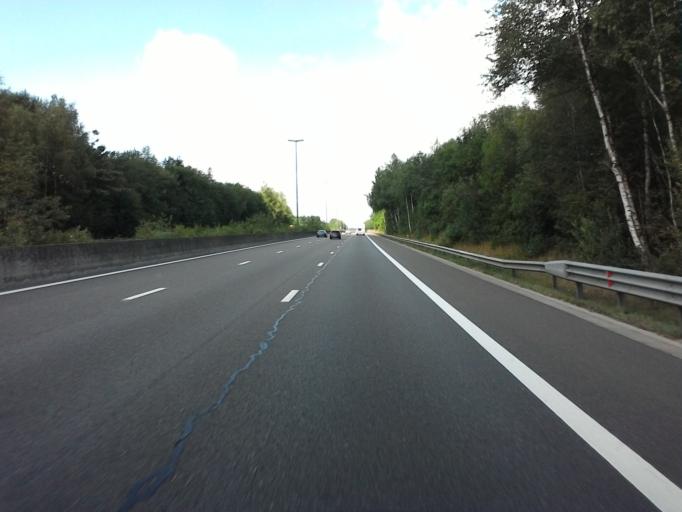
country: BE
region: Wallonia
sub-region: Province du Luxembourg
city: Habay-la-Vieille
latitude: 49.6970
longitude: 5.6633
